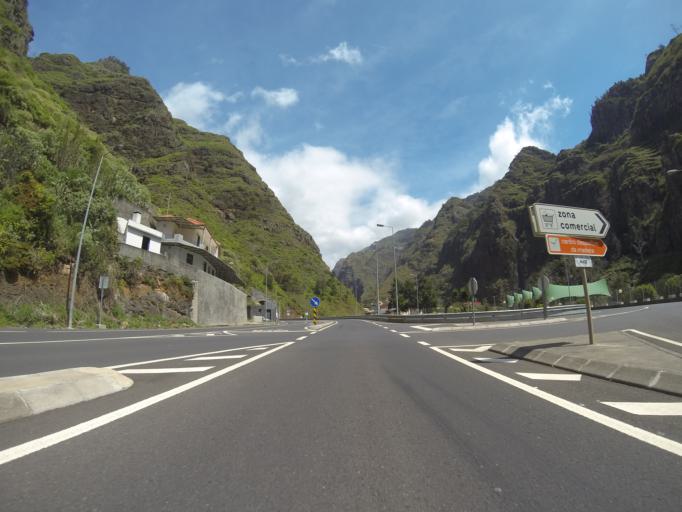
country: PT
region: Madeira
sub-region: Ribeira Brava
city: Campanario
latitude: 32.6914
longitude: -17.0487
